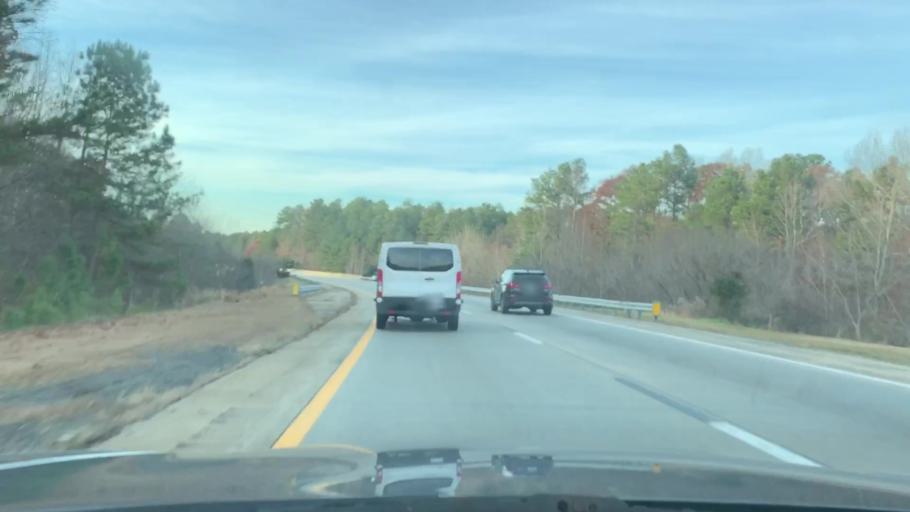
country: US
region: North Carolina
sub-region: Orange County
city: Hillsborough
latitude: 36.0577
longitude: -79.1248
